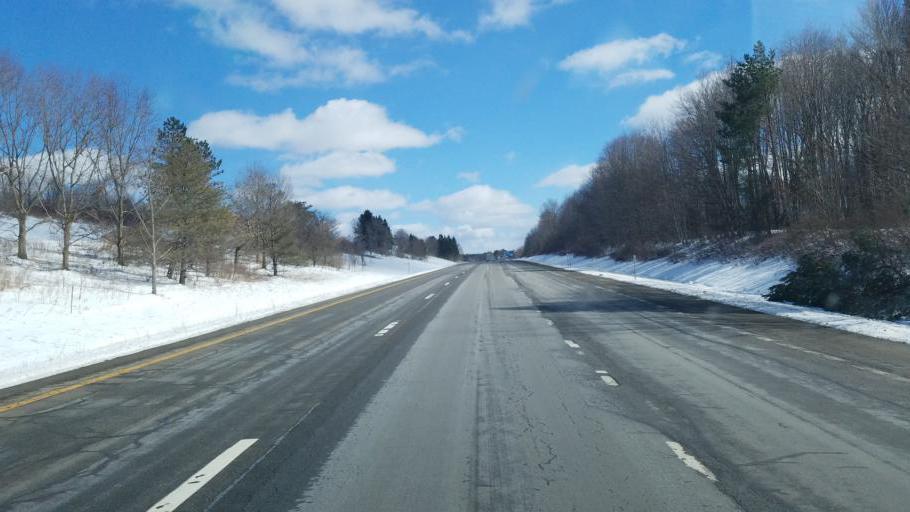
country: US
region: New York
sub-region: Chautauqua County
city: Celoron
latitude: 42.1237
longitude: -79.2676
